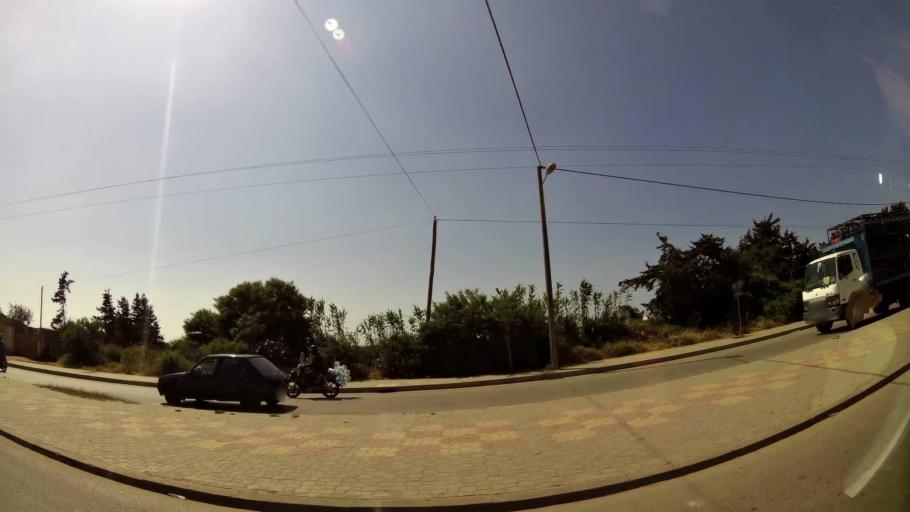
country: MA
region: Rabat-Sale-Zemmour-Zaer
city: Sale
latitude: 34.0703
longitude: -6.7590
